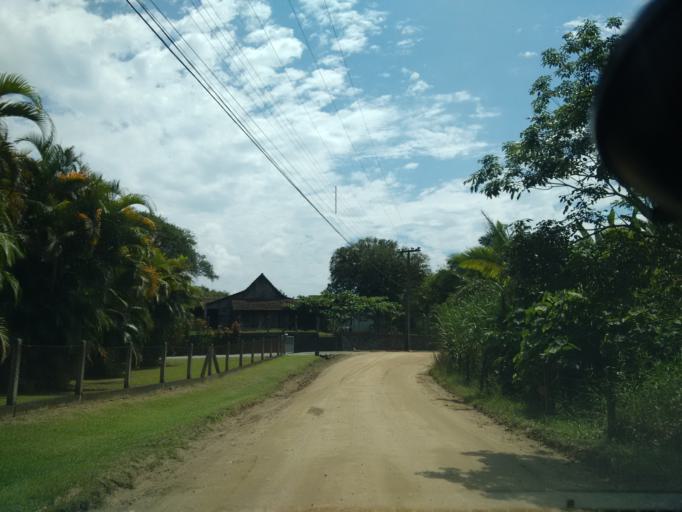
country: BR
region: Santa Catarina
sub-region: Indaial
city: Indaial
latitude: -26.8477
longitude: -49.1596
